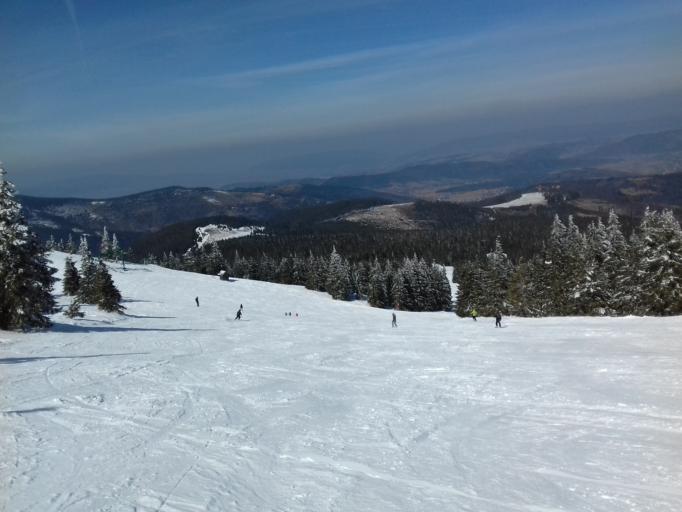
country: PL
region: Silesian Voivodeship
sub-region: Powiat zywiecki
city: Korbielow
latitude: 49.5356
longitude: 19.3175
